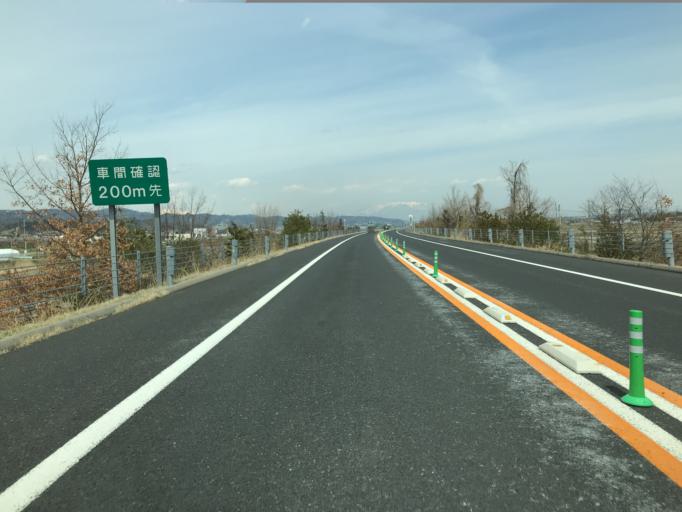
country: JP
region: Yamagata
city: Kaminoyama
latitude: 38.2315
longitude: 140.2755
